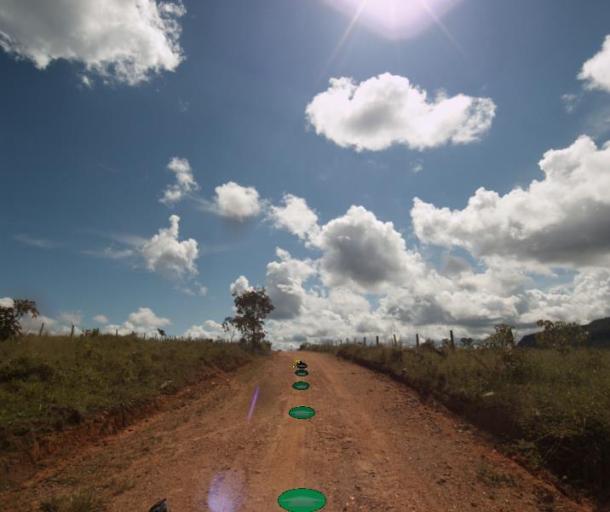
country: BR
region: Goias
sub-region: Pirenopolis
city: Pirenopolis
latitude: -15.7857
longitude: -48.9237
